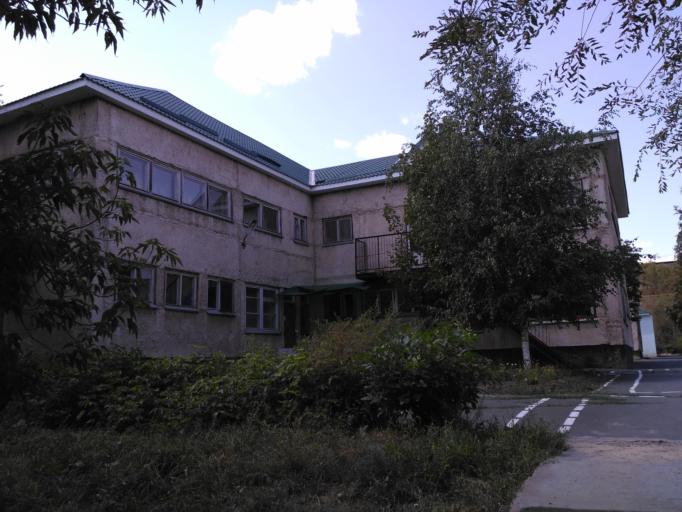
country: RU
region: Orenburg
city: Novotroitsk
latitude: 51.1869
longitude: 58.2818
